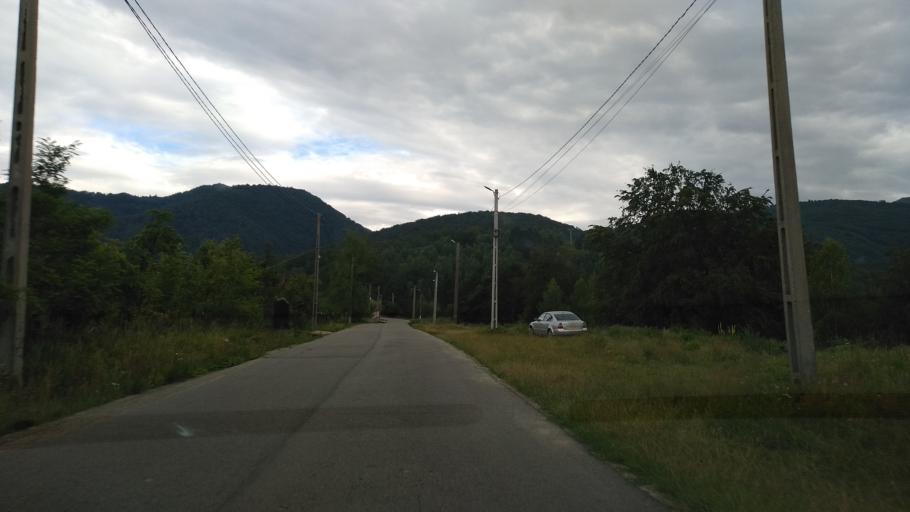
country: RO
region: Hunedoara
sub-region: Municipiul  Vulcan
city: Jiu-Paroseni
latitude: 45.3582
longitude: 23.2881
